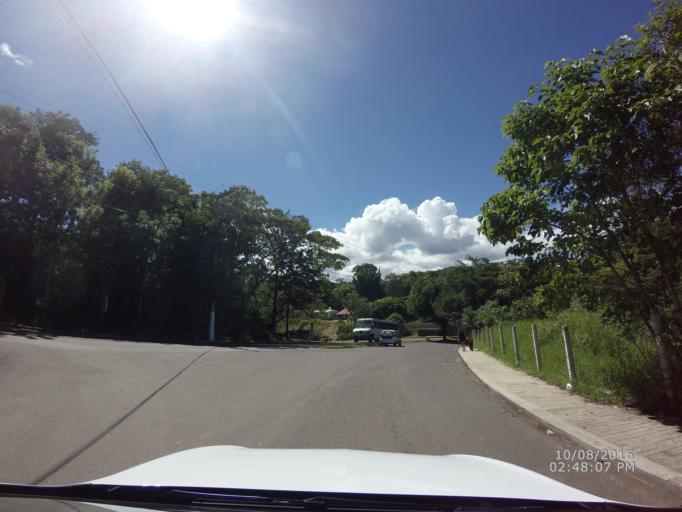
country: MX
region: Veracruz
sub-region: Xalapa
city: Lomas Verdes
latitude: 19.5047
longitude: -96.8907
